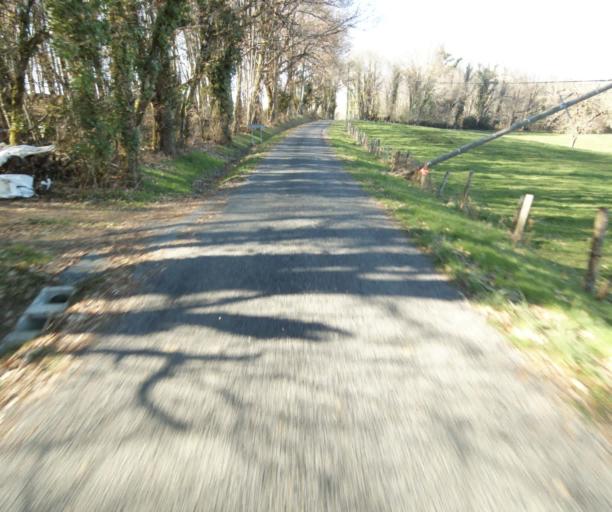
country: FR
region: Limousin
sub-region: Departement de la Correze
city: Chamboulive
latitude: 45.4017
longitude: 1.6635
